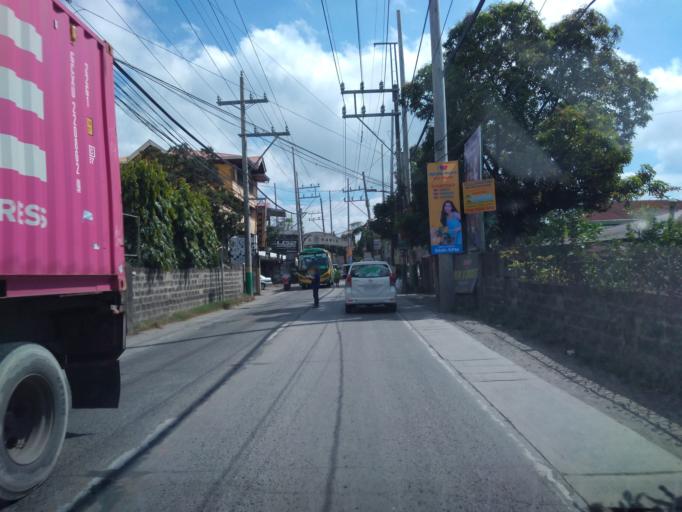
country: PH
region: Central Luzon
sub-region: Province of Bulacan
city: Bocaue
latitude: 14.8084
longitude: 120.9454
